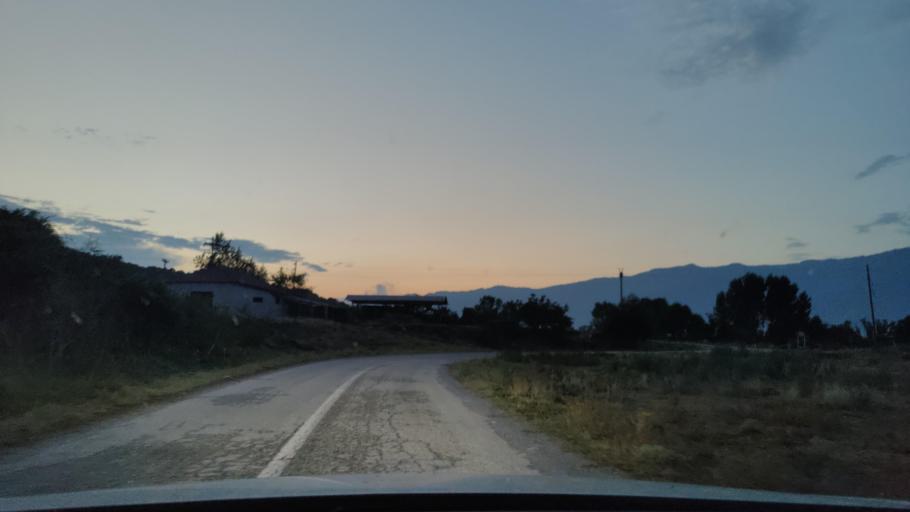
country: GR
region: Central Macedonia
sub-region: Nomos Serron
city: Chrysochorafa
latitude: 41.2046
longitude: 23.0756
